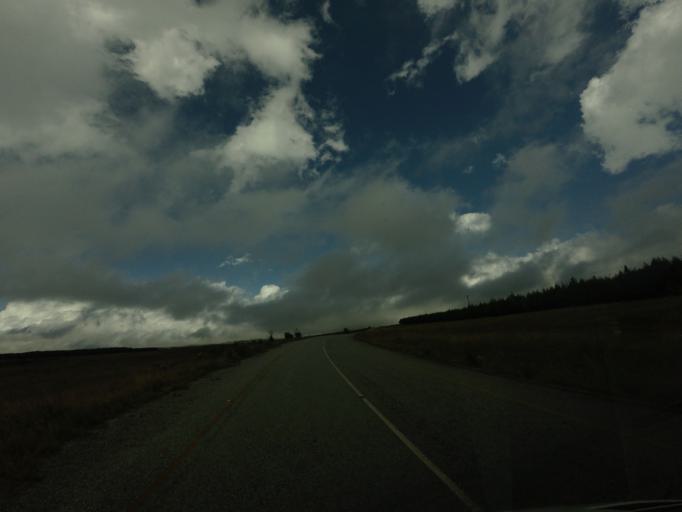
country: ZA
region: Mpumalanga
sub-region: Ehlanzeni District
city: Graksop
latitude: -24.8570
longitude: 30.8708
